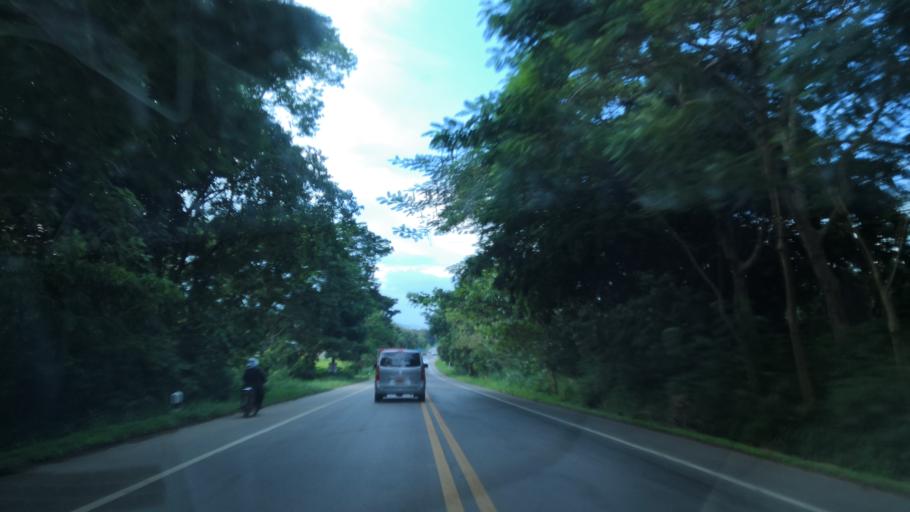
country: TH
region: Chiang Rai
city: Wiang Pa Pao
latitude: 19.4715
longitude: 99.4855
